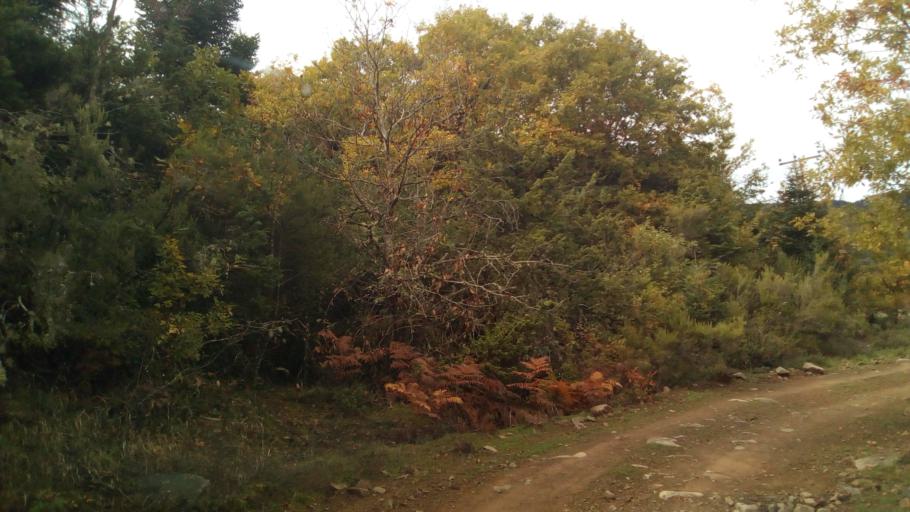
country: GR
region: West Greece
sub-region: Nomos Aitolias kai Akarnanias
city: Nafpaktos
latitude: 38.5586
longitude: 21.9642
